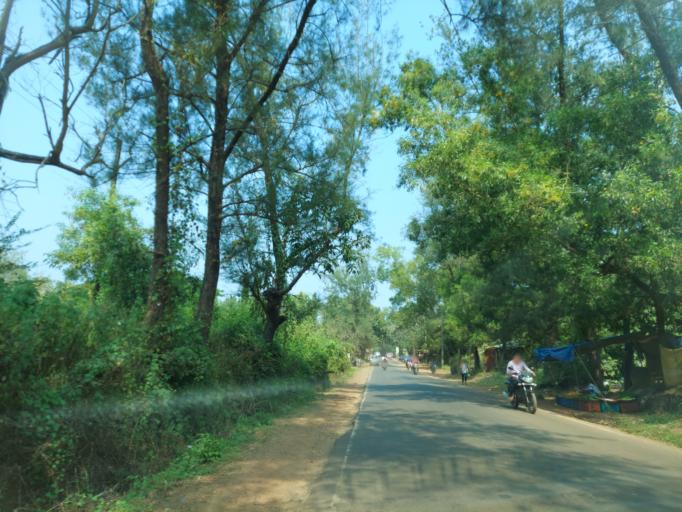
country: IN
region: Maharashtra
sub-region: Sindhudurg
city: Kudal
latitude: 15.9982
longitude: 73.6854
